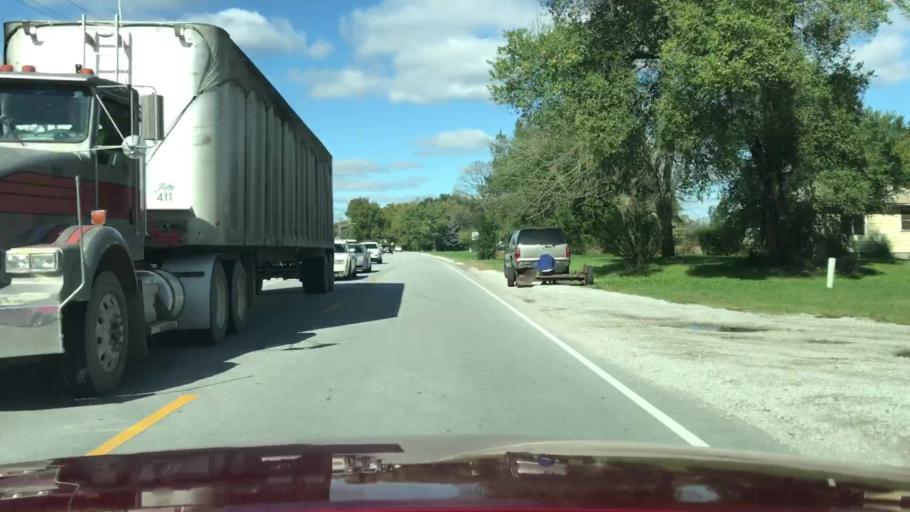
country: US
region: Illinois
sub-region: Cook County
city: Lynwood
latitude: 41.5144
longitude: -87.5394
